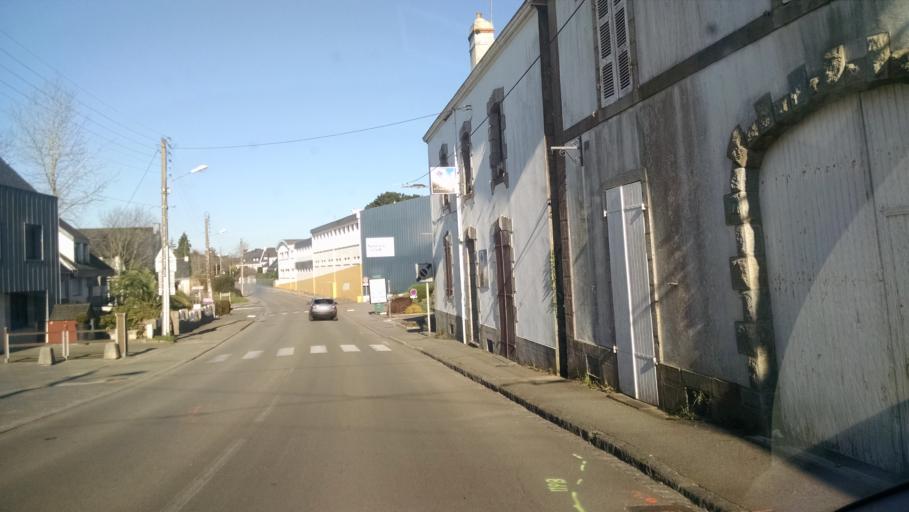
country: FR
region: Brittany
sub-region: Departement du Morbihan
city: Guidel-Plage
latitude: 47.7903
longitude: -3.4891
